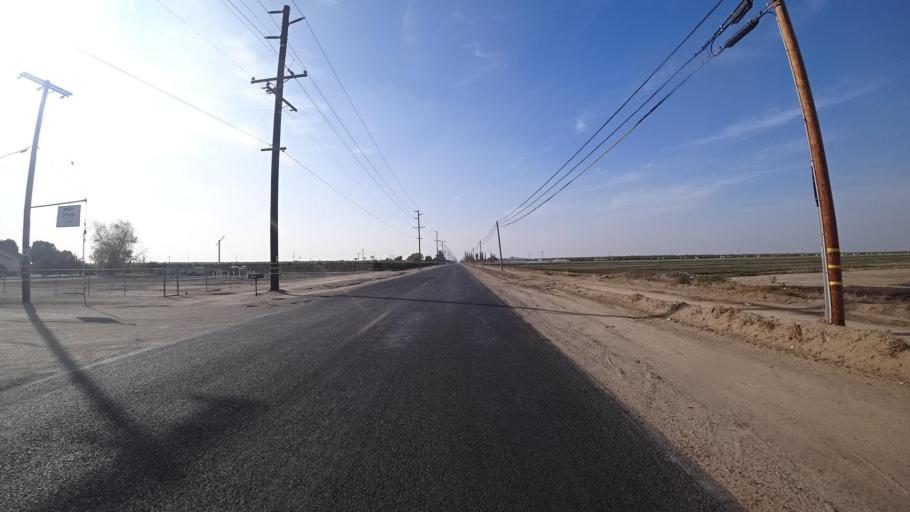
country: US
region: California
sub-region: Kern County
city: Delano
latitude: 35.7759
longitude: -119.2005
